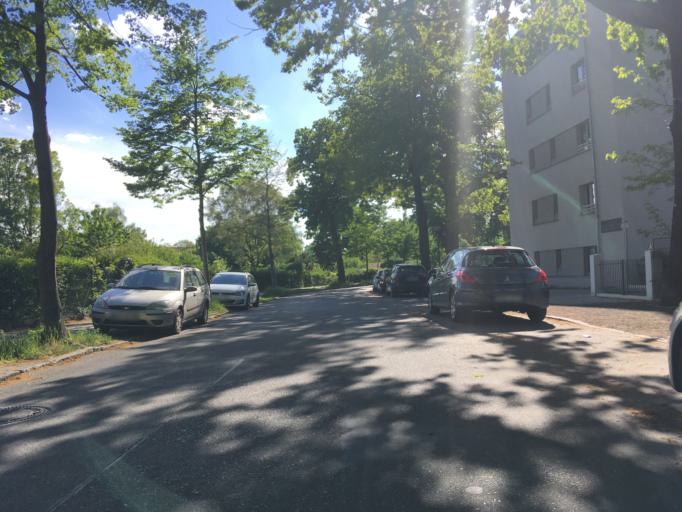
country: DE
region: Berlin
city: Oberschoneweide
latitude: 52.4530
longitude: 13.5377
